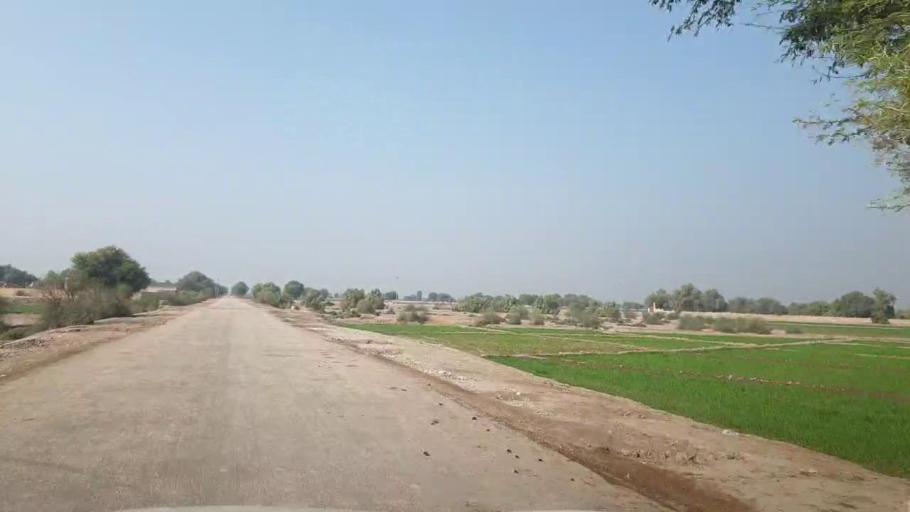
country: PK
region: Sindh
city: Bhan
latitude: 26.5078
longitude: 67.7911
